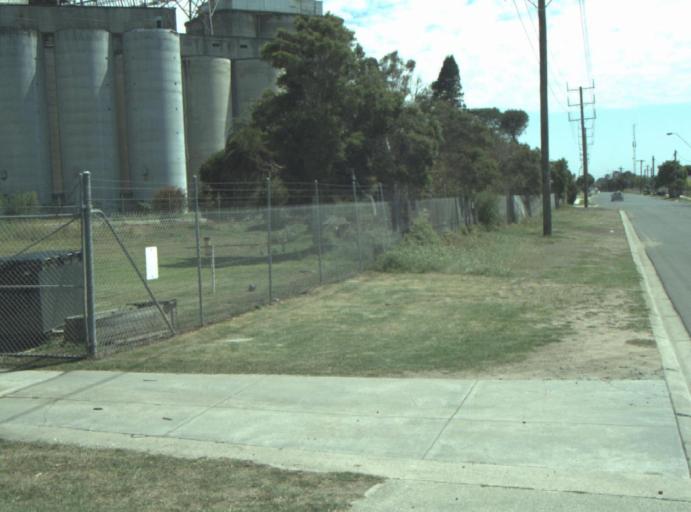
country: AU
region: Victoria
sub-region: Greater Geelong
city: Hamlyn Heights
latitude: -38.1404
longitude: 144.3180
